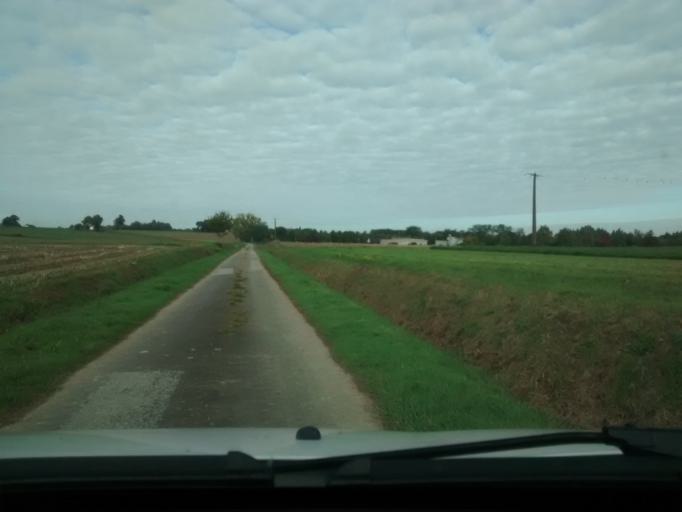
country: FR
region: Brittany
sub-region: Departement d'Ille-et-Vilaine
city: Chavagne
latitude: 48.0783
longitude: -1.7607
